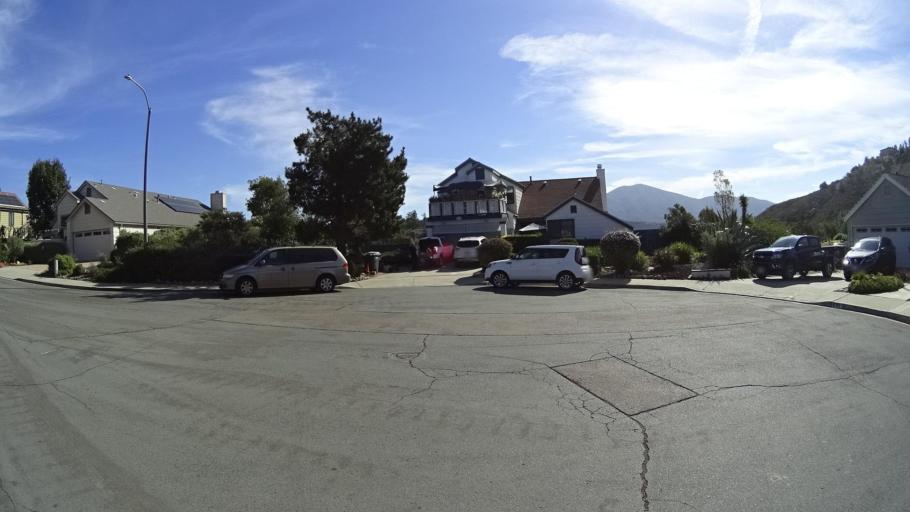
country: US
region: California
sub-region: San Diego County
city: Spring Valley
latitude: 32.7282
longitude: -116.9852
